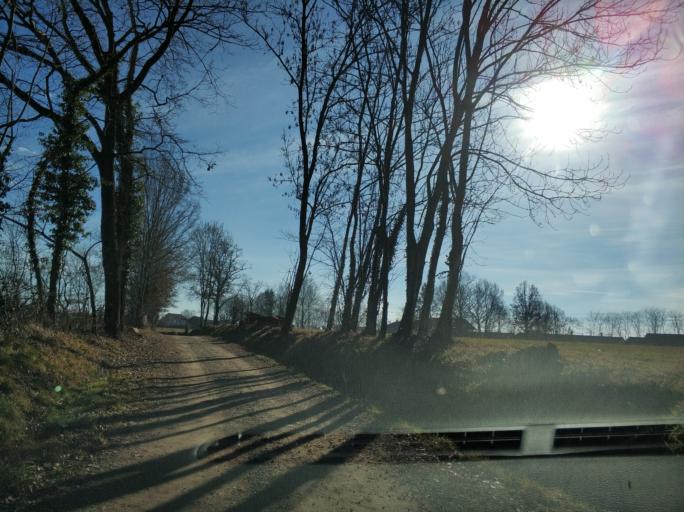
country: IT
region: Piedmont
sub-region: Provincia di Torino
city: San Carlo Canavese
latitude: 45.2542
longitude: 7.6065
